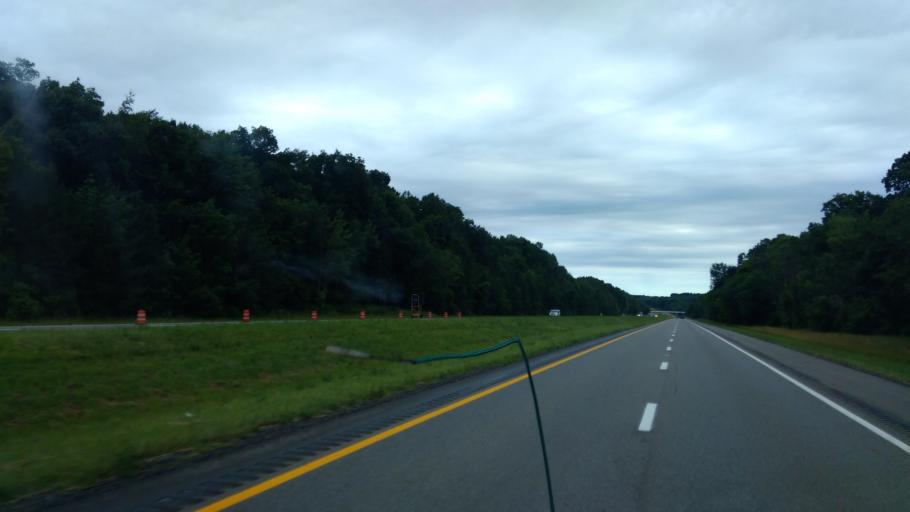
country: US
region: Ohio
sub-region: Mahoning County
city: Canfield
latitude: 40.9753
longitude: -80.7208
